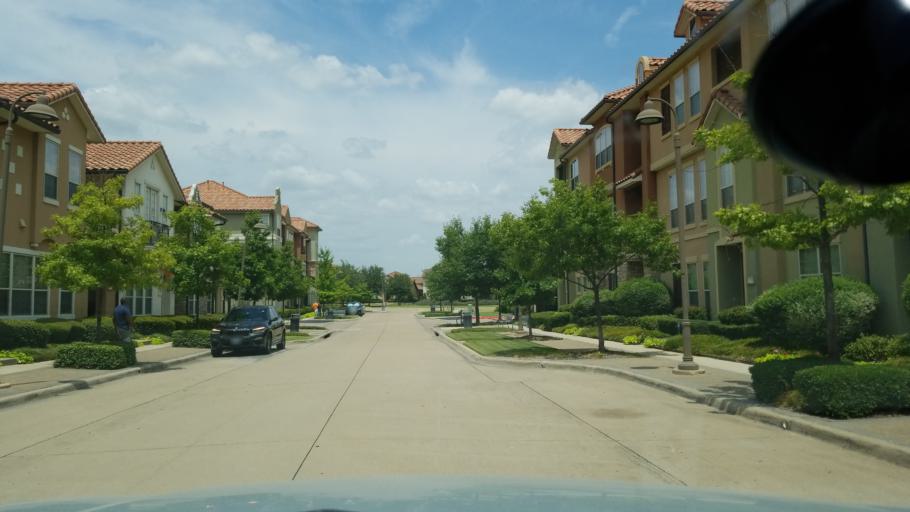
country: US
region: Texas
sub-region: Dallas County
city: Farmers Branch
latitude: 32.9019
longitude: -96.9347
